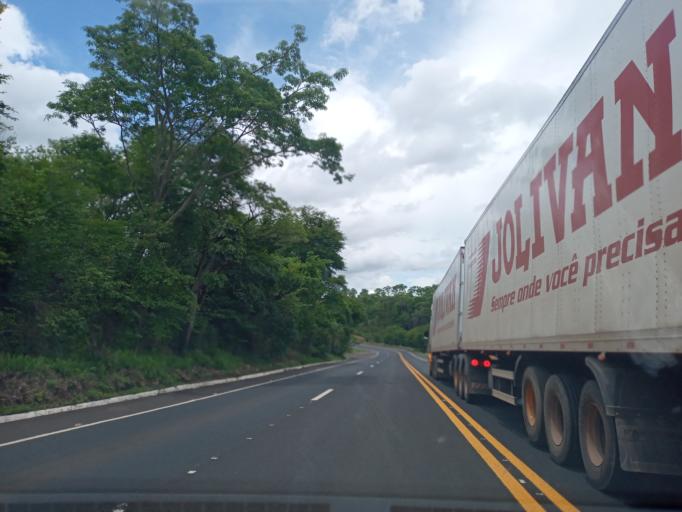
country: BR
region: Minas Gerais
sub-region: Uberaba
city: Uberaba
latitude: -19.2834
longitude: -47.6239
